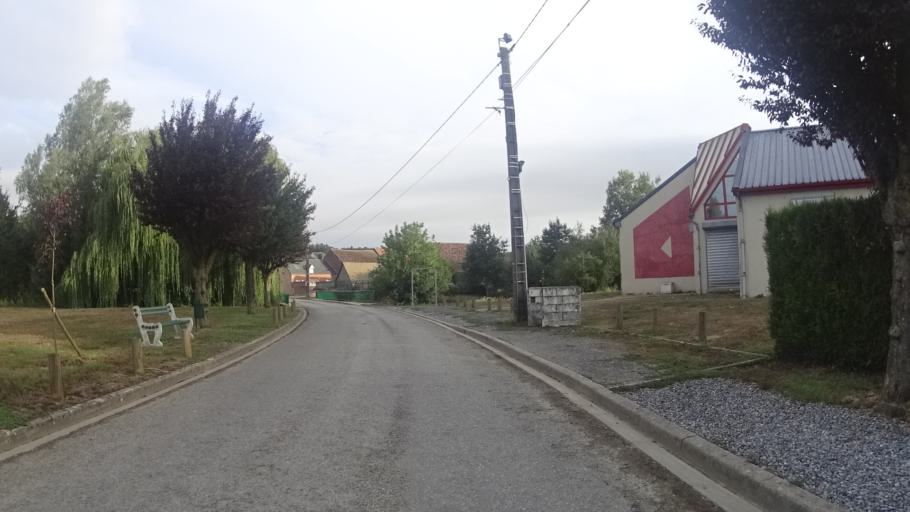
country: FR
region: Picardie
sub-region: Departement de l'Aisne
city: Origny-Sainte-Benoite
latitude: 49.8279
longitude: 3.4677
